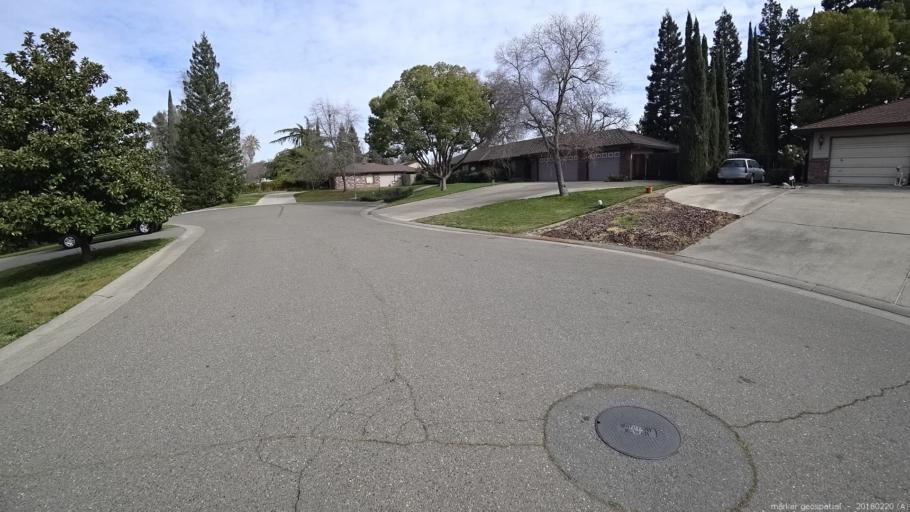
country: US
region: California
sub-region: Sacramento County
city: Orangevale
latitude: 38.6841
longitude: -121.2285
